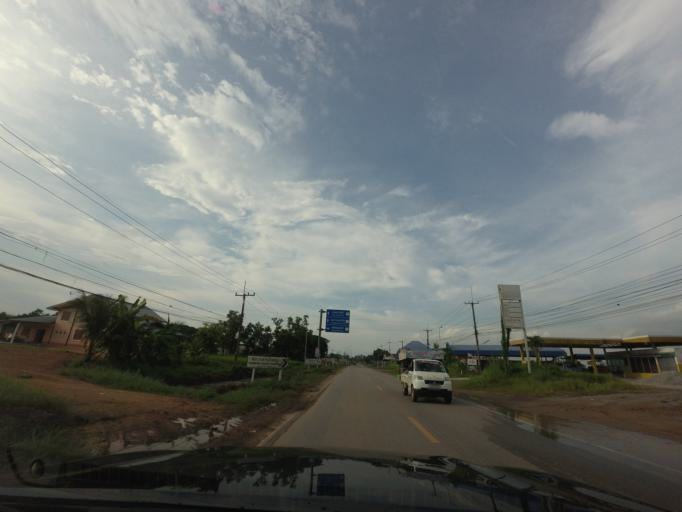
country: TH
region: Nong Khai
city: Pho Tak
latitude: 17.7736
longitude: 102.3957
